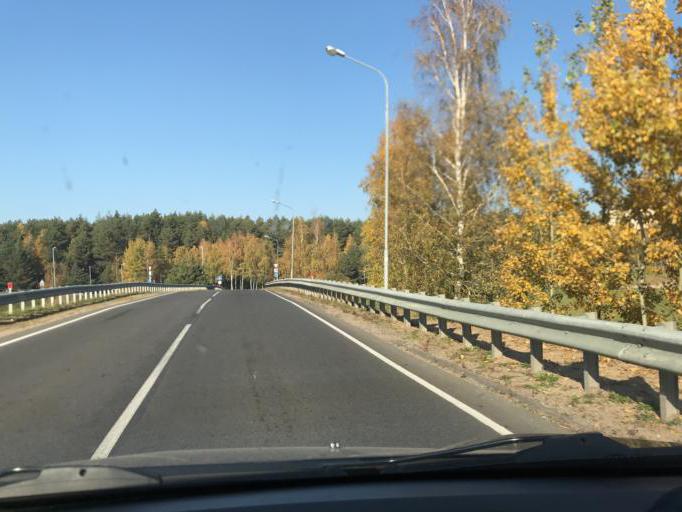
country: BY
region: Minsk
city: Pryvol'ny
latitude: 53.8223
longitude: 27.7609
